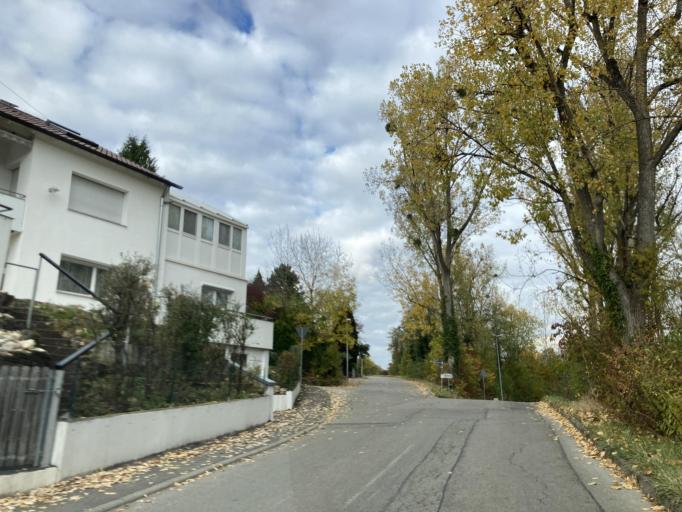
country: DE
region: Baden-Wuerttemberg
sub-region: Tuebingen Region
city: Dusslingen
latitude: 48.4560
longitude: 9.0556
